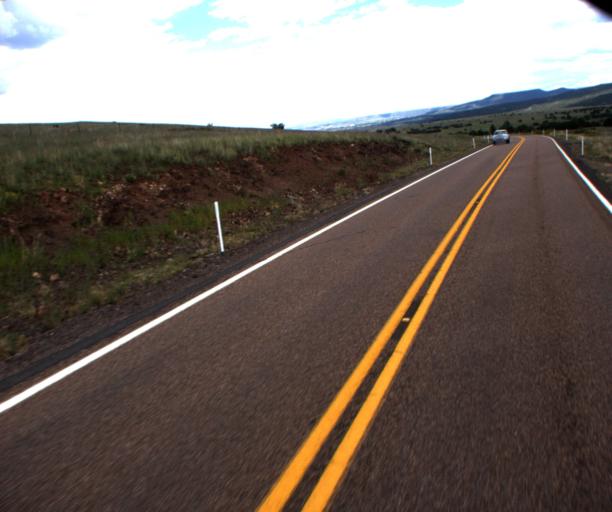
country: US
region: Arizona
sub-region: Apache County
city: Eagar
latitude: 34.0939
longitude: -109.4279
